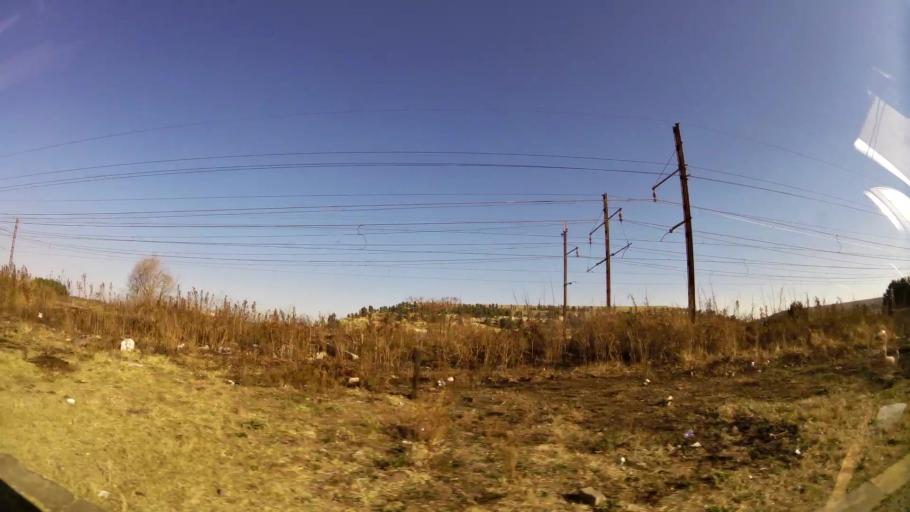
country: ZA
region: Gauteng
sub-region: City of Johannesburg Metropolitan Municipality
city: Johannesburg
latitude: -26.2165
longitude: 27.9769
